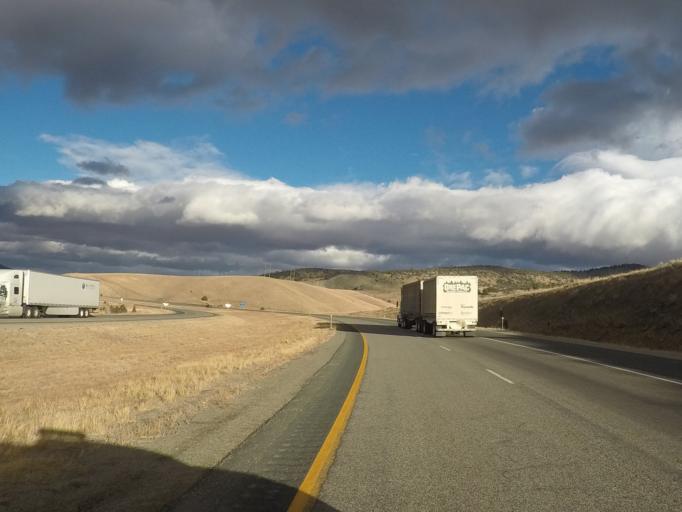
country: US
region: Montana
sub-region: Jefferson County
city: Whitehall
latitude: 45.8791
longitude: -111.8763
